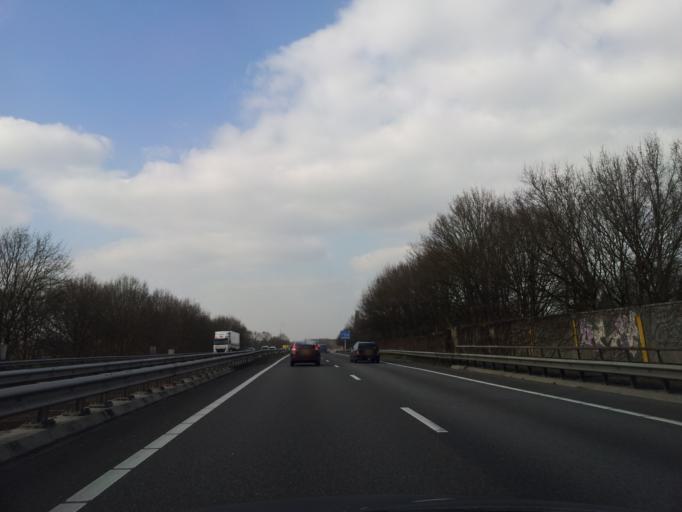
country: NL
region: North Brabant
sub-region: Gemeente Cranendonck
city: Cranendonck
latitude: 51.3121
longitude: 5.6063
